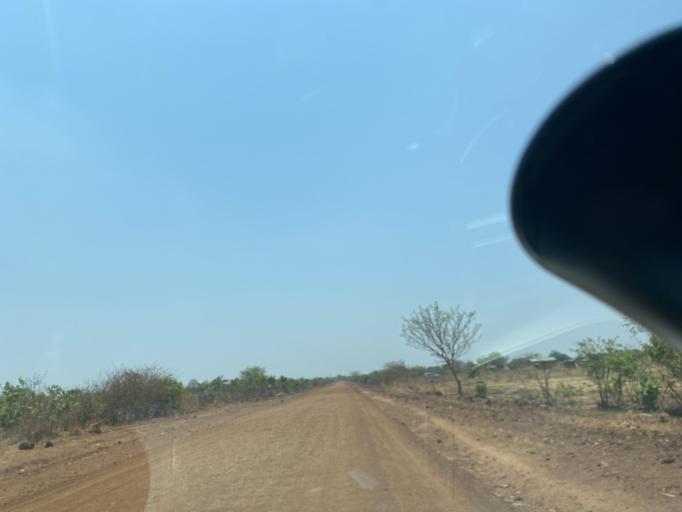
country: ZM
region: Lusaka
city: Lusaka
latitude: -15.4559
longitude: 27.9404
